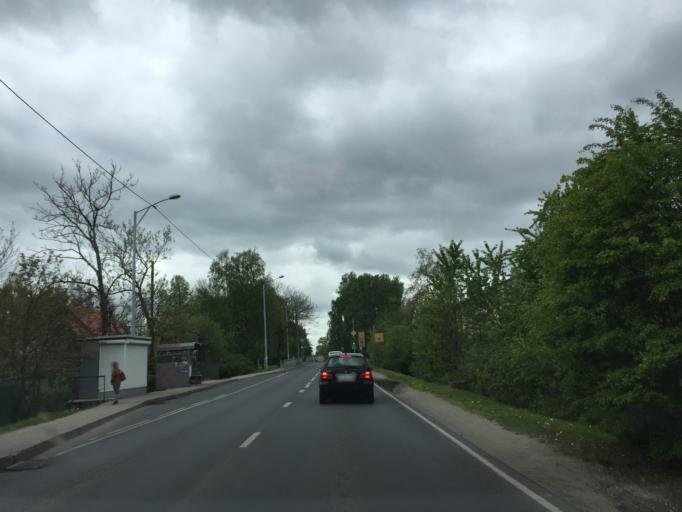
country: RU
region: Kaliningrad
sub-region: Gorod Kaliningrad
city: Kaliningrad
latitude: 54.6779
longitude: 20.4454
